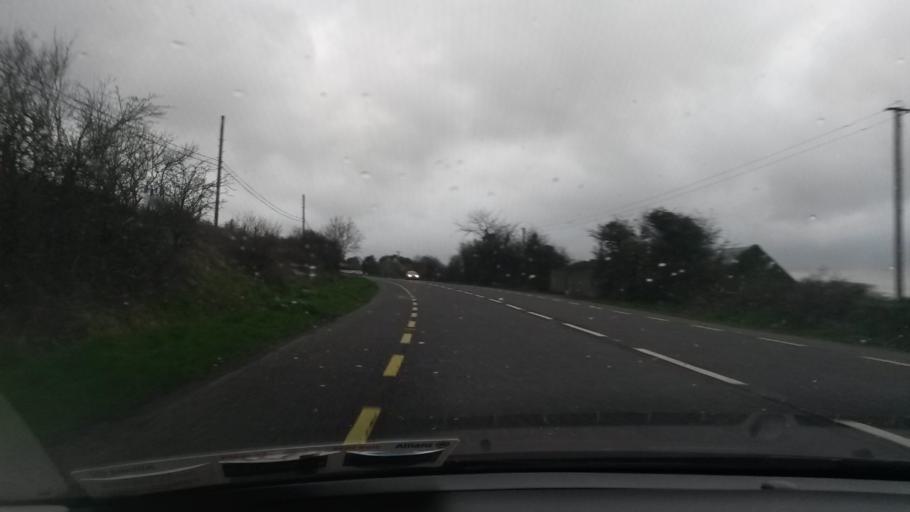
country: IE
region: Munster
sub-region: County Limerick
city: Abbeyfeale
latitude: 52.3678
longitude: -9.3212
